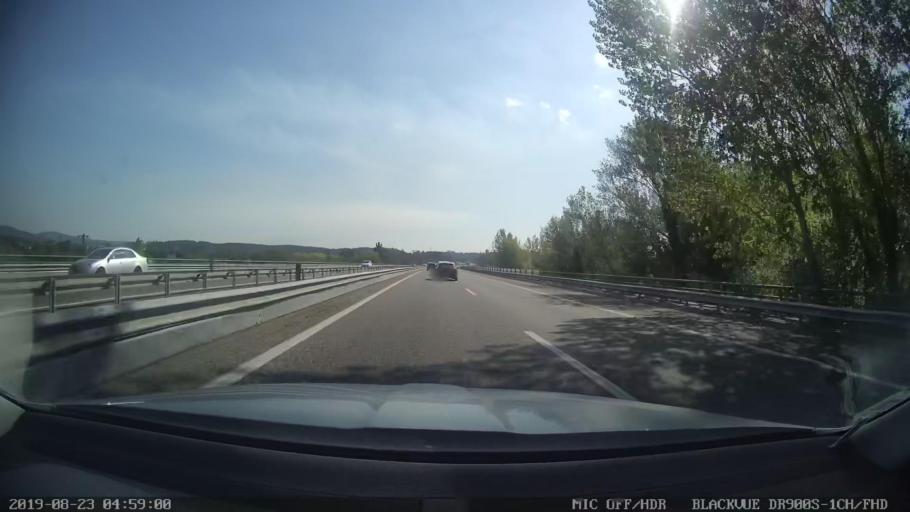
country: PT
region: Coimbra
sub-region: Soure
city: Soure
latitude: 40.0212
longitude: -8.5938
